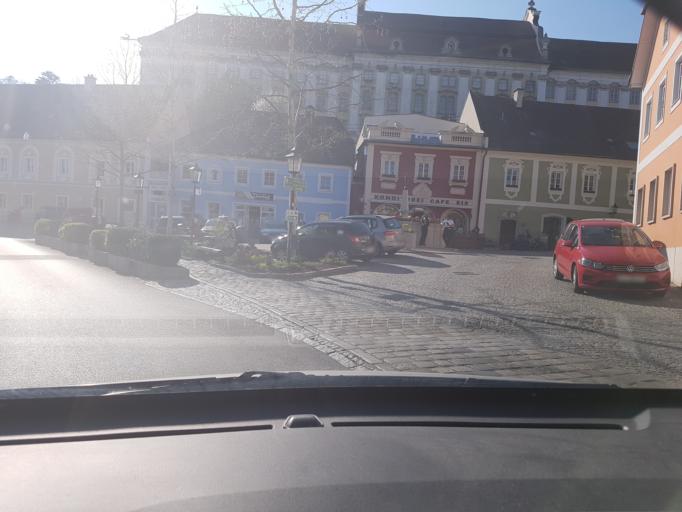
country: AT
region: Upper Austria
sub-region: Politischer Bezirk Linz-Land
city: Sankt Florian
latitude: 48.2064
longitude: 14.3807
